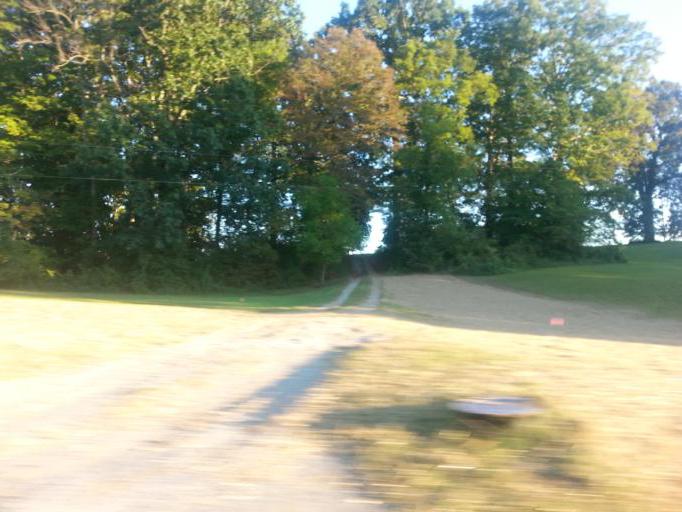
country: US
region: Tennessee
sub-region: Knox County
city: Knoxville
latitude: 35.8969
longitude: -83.8621
